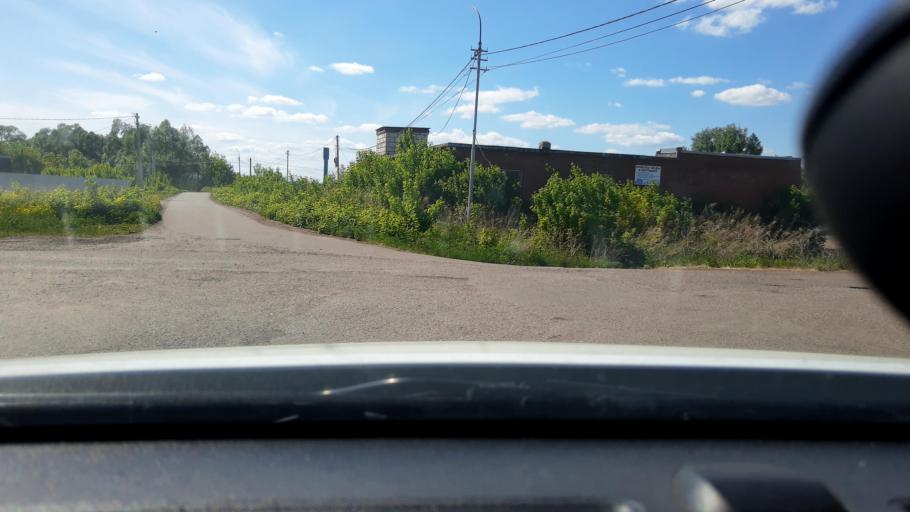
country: RU
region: Bashkortostan
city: Avdon
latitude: 54.5055
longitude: 55.8152
